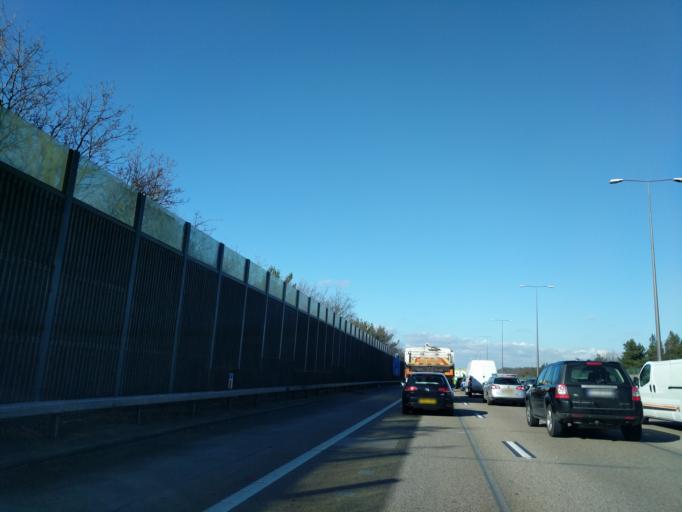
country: GB
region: England
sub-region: Surrey
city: Addlestone
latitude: 51.3520
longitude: -0.4891
